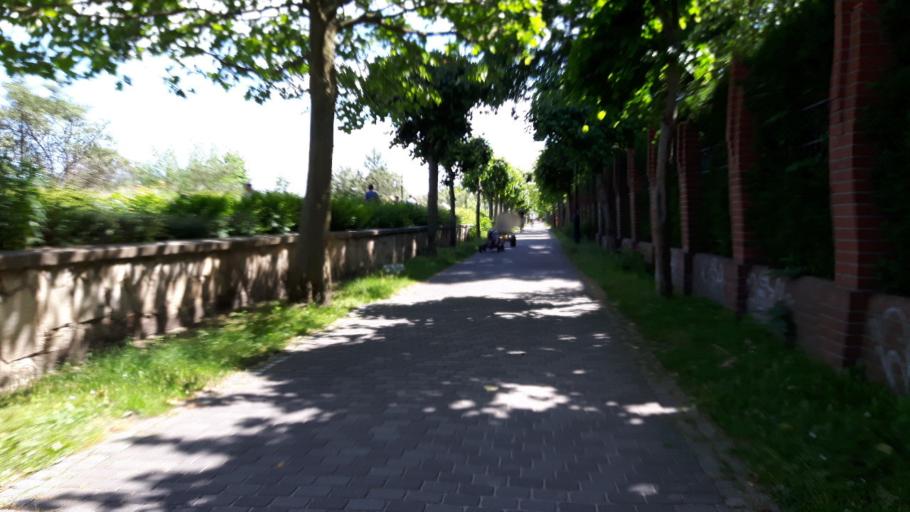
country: PL
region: Pomeranian Voivodeship
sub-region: Sopot
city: Sopot
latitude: 54.4418
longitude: 18.5746
